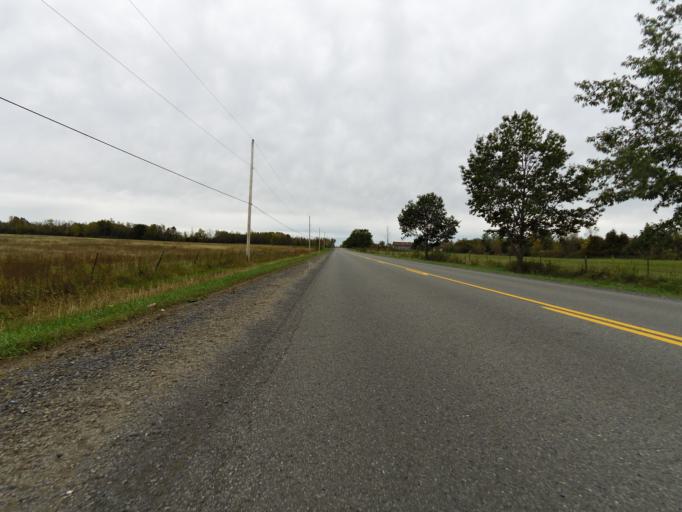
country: CA
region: Ontario
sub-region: Lanark County
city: Smiths Falls
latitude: 44.8367
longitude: -75.8168
